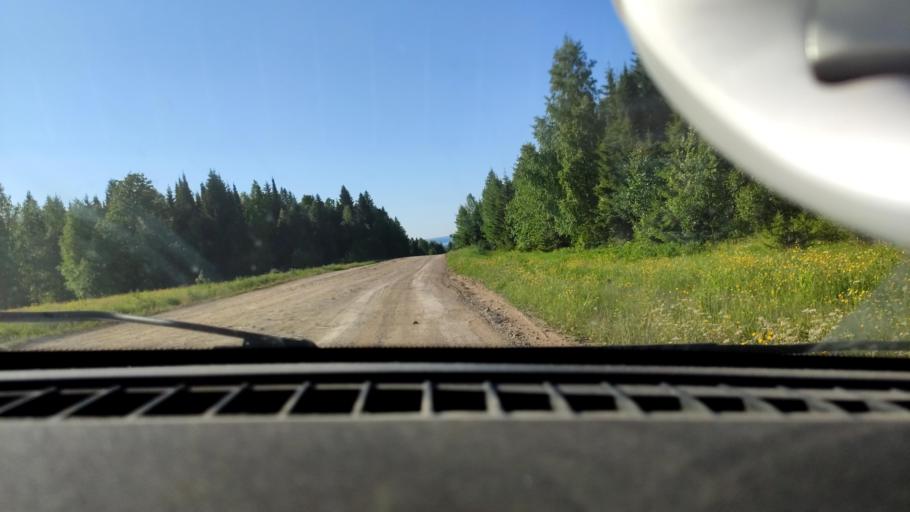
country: RU
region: Perm
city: Novyye Lyady
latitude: 58.1796
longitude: 56.5896
